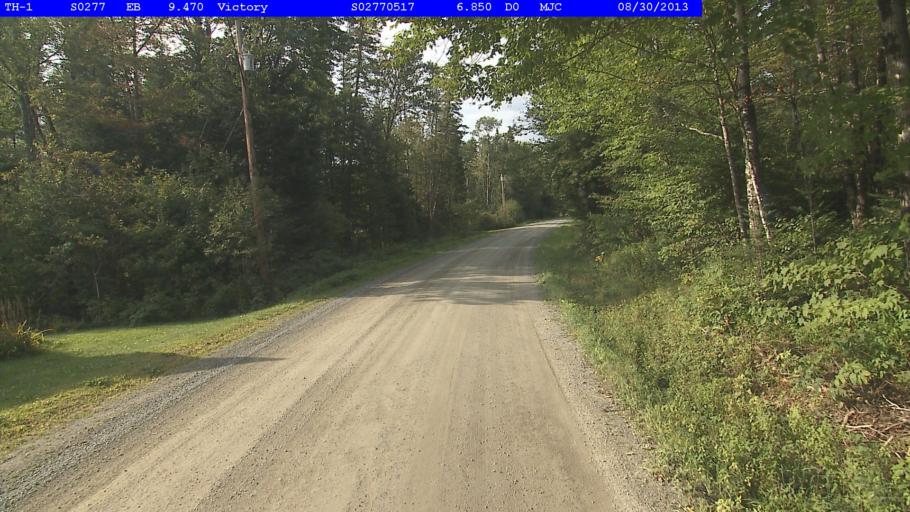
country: US
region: Vermont
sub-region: Caledonia County
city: Lyndonville
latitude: 44.5666
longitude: -71.7891
